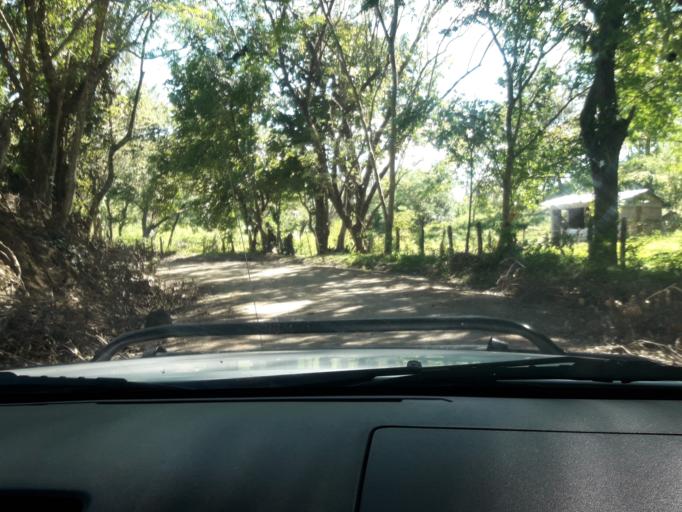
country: NI
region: Rivas
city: Cardenas
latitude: 11.2313
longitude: -85.6491
